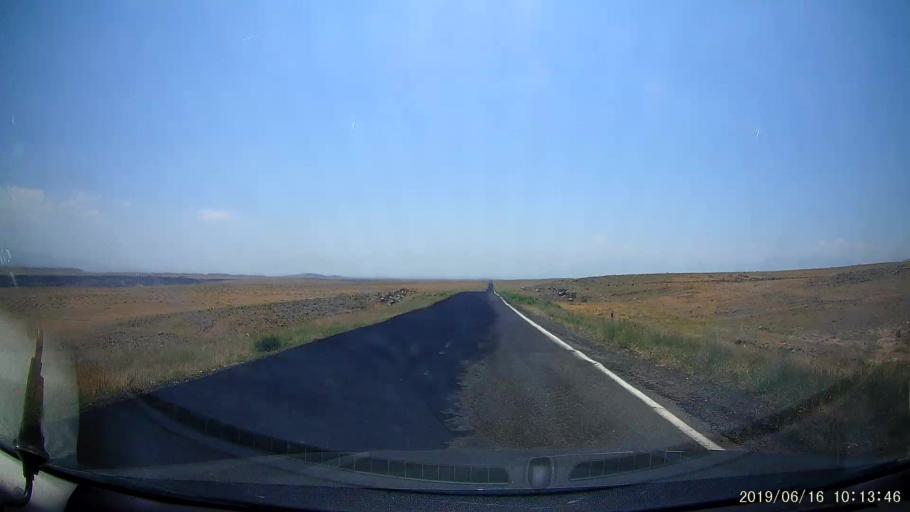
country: TR
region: Igdir
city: Tuzluca
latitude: 40.1906
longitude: 43.6491
